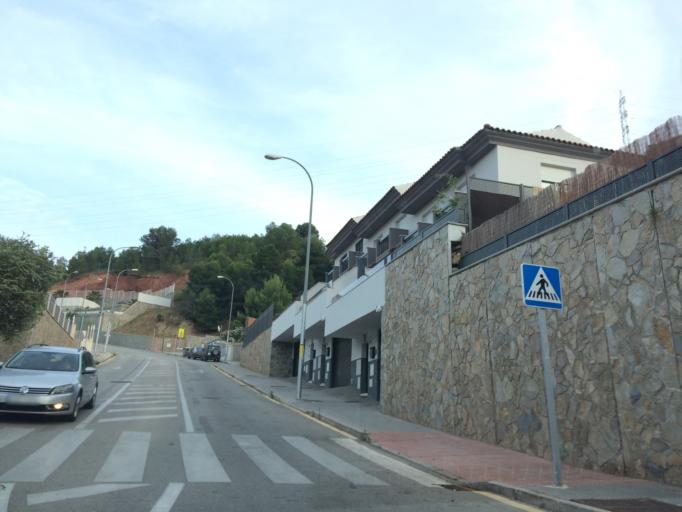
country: ES
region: Andalusia
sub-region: Provincia de Malaga
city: Malaga
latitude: 36.7323
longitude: -4.3934
